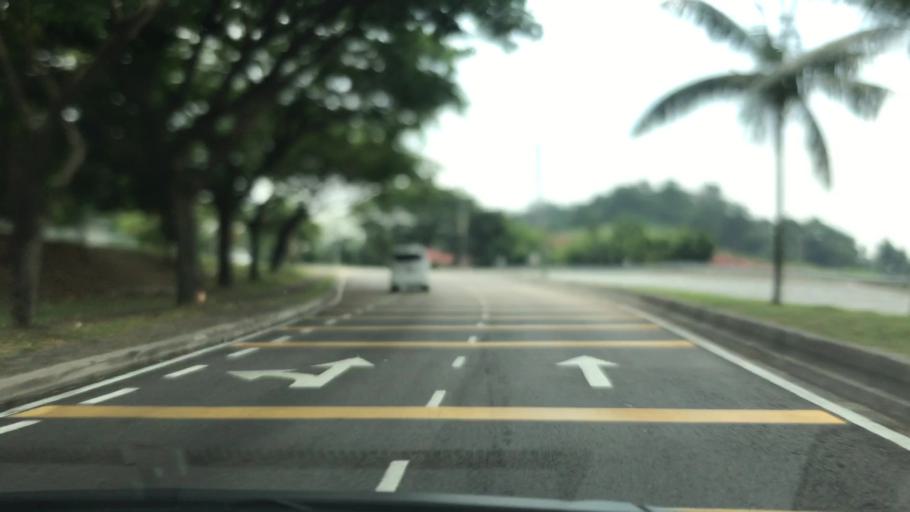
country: MY
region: Selangor
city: Kampong Baharu Balakong
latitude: 3.0247
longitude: 101.6792
